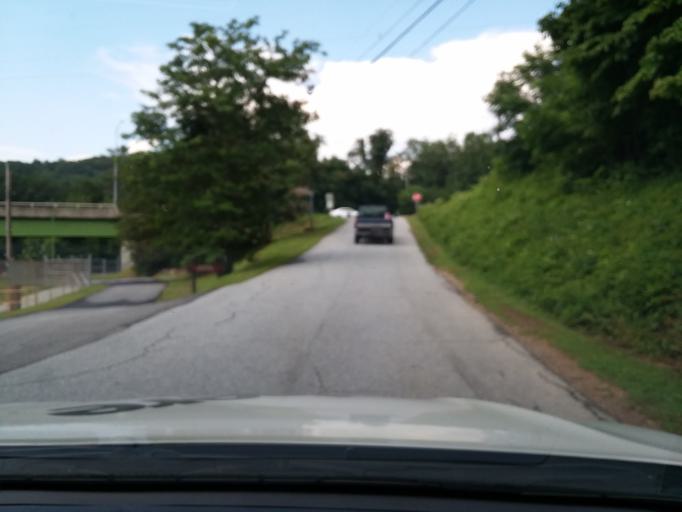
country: US
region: Georgia
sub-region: Rabun County
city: Clayton
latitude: 34.7381
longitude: -83.3950
